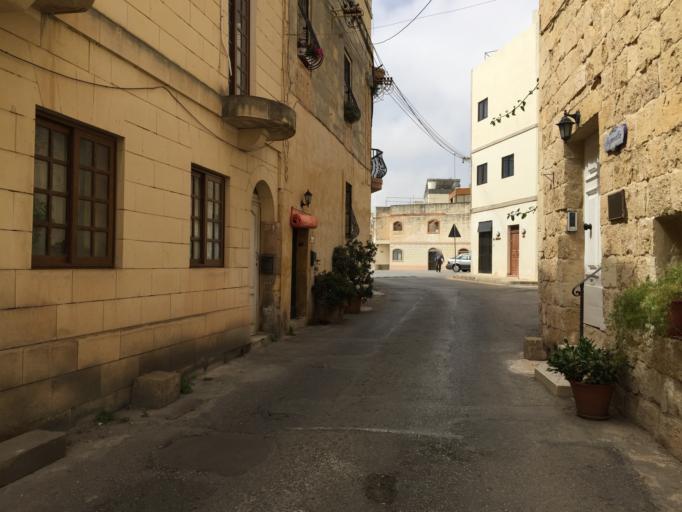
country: MT
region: Haz-Zabbar
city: Zabbar
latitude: 35.8731
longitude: 14.5383
